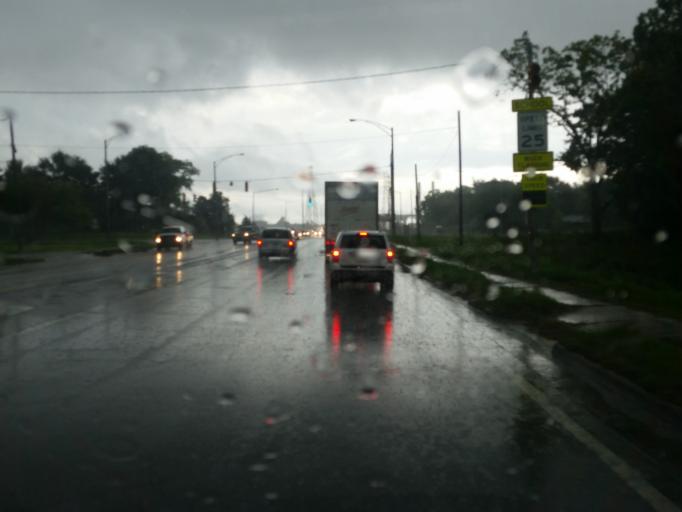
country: US
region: Alabama
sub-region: Mobile County
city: Prichard
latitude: 30.7323
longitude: -88.0579
